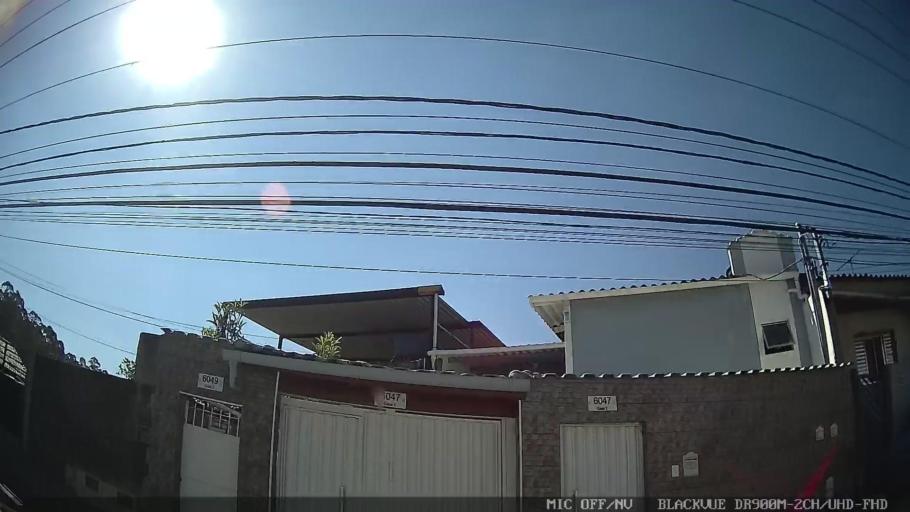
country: BR
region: Sao Paulo
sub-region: Ferraz De Vasconcelos
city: Ferraz de Vasconcelos
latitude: -23.5523
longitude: -46.4702
